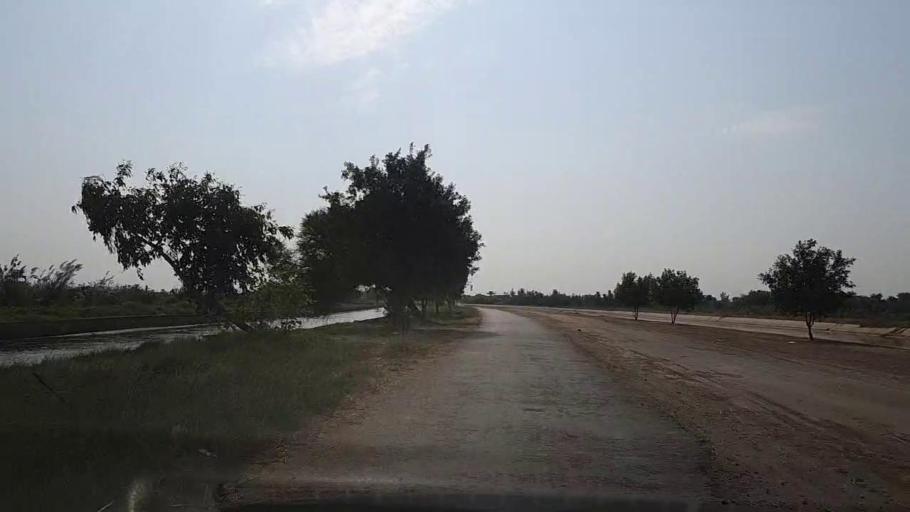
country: PK
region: Sindh
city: Thatta
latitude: 24.7456
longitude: 67.7670
